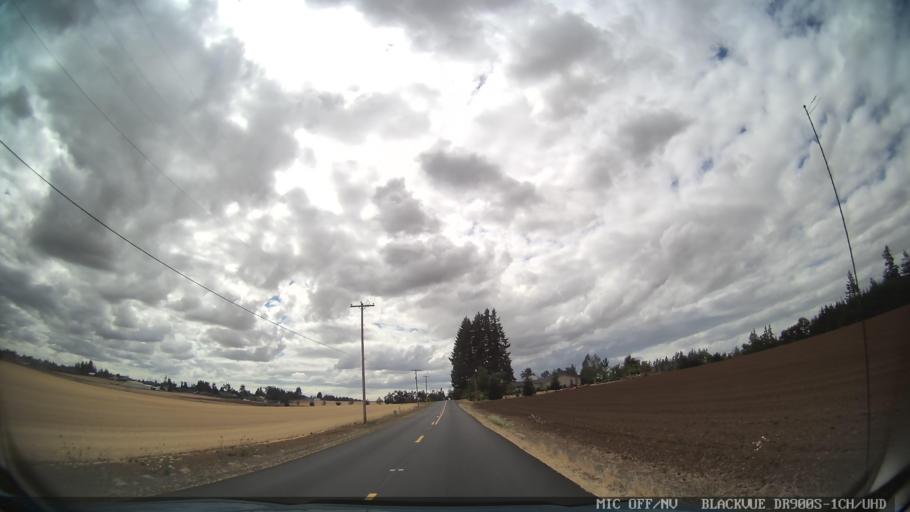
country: US
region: Oregon
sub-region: Marion County
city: Sublimity
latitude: 44.8405
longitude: -122.7768
